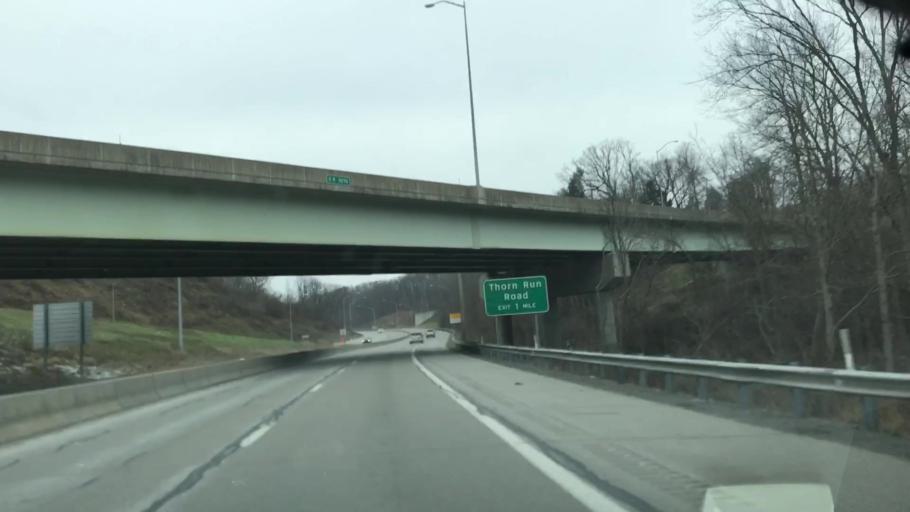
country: US
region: Pennsylvania
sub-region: Allegheny County
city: Carnot-Moon
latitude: 40.4811
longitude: -80.2015
